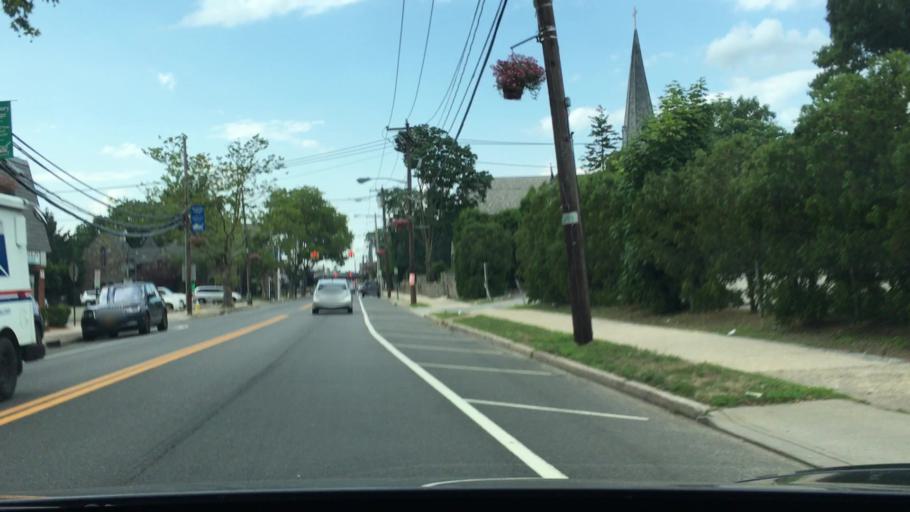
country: US
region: New York
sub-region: Nassau County
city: Westbury
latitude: 40.7496
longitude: -73.5877
